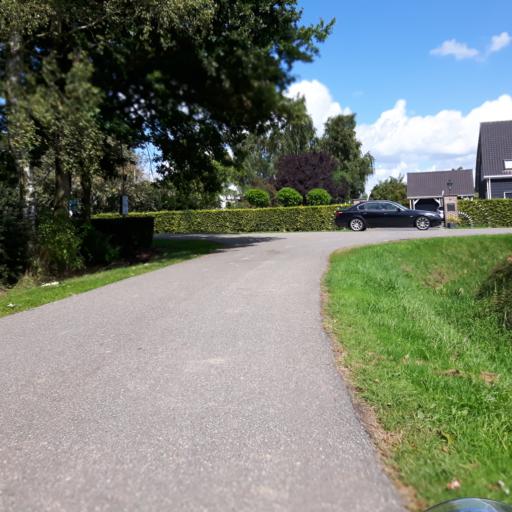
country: NL
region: Zeeland
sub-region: Gemeente Goes
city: Goes
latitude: 51.4529
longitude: 3.8550
